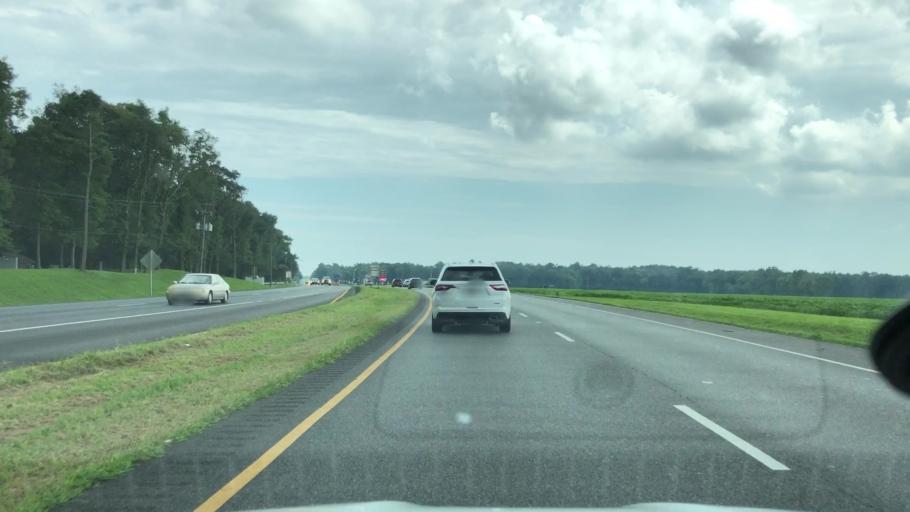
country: US
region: Maryland
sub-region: Worcester County
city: Pocomoke City
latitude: 38.0051
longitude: -75.5445
